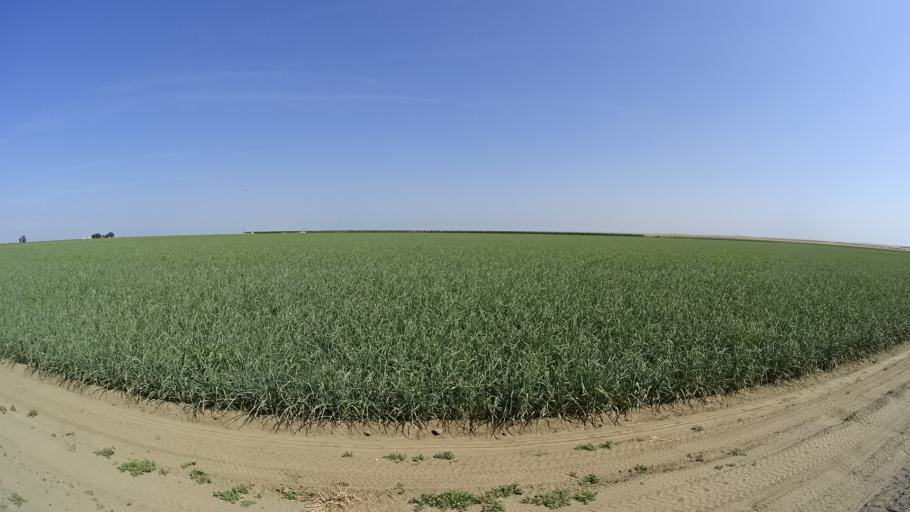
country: US
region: California
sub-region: Kings County
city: Kettleman City
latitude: 36.0363
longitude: -119.9816
